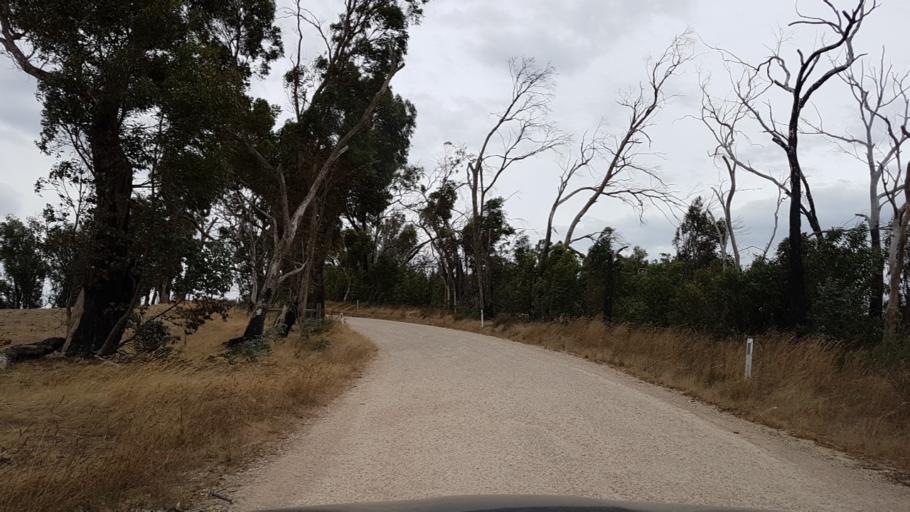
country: AU
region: South Australia
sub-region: Adelaide Hills
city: Gumeracha
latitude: -34.8000
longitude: 138.8176
